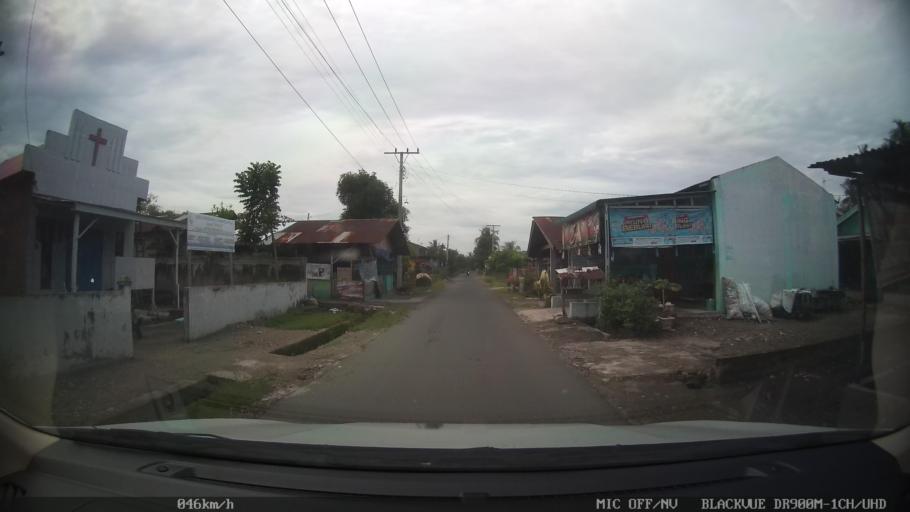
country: ID
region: North Sumatra
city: Sunggal
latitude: 3.5817
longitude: 98.5775
